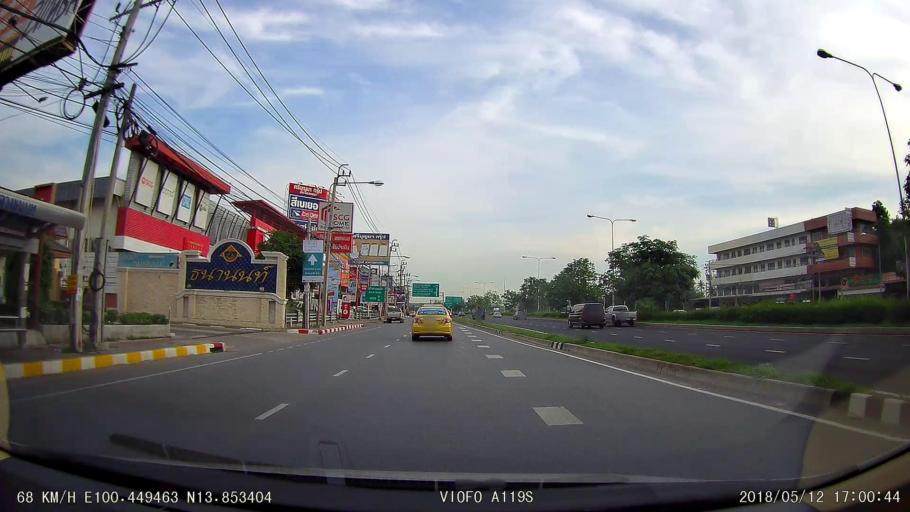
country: TH
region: Nonthaburi
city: Bang Kruai
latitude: 13.8533
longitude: 100.4494
